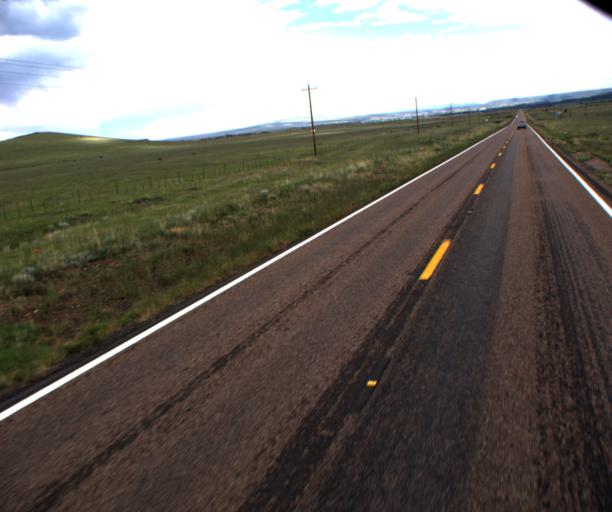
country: US
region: Arizona
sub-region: Apache County
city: Eagar
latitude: 34.1010
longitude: -109.3817
